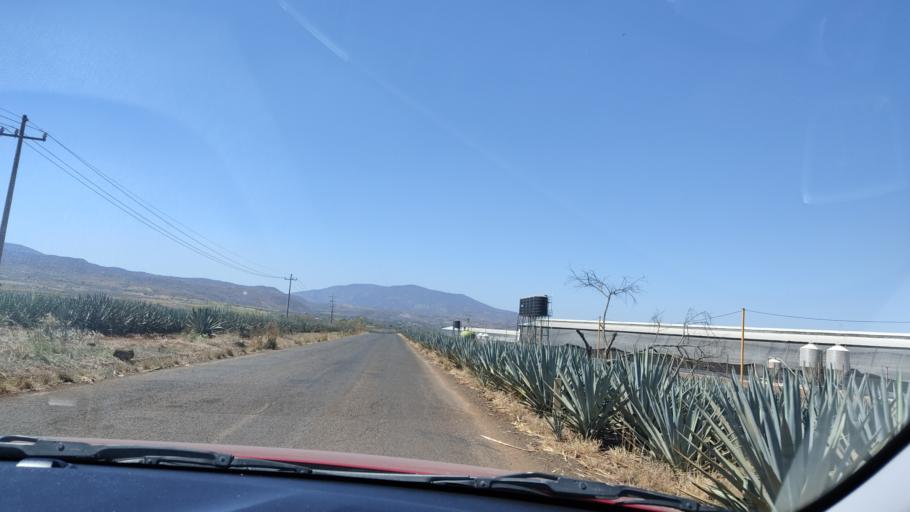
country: MX
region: Nayarit
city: Santa Maria del Oro
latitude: 21.4378
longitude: -104.6219
